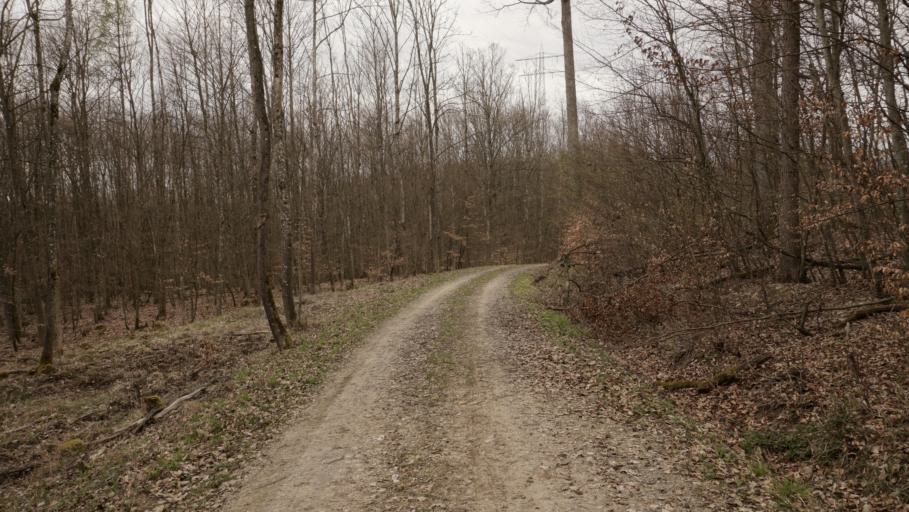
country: DE
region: Baden-Wuerttemberg
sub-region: Karlsruhe Region
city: Mosbach
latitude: 49.3791
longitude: 9.1445
